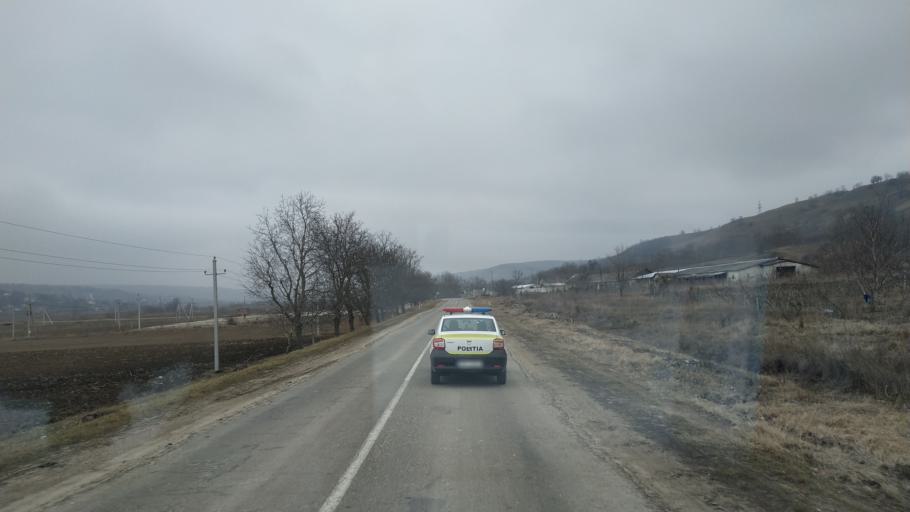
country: MD
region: Hincesti
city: Hincesti
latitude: 46.9702
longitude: 28.4757
